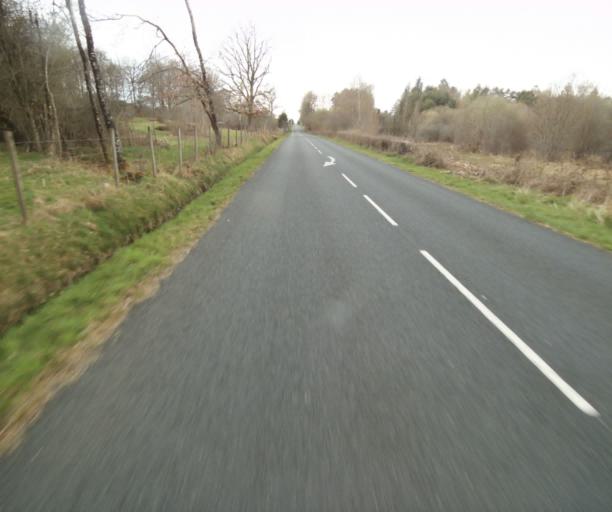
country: FR
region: Limousin
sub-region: Departement de la Correze
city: Egletons
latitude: 45.2772
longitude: 1.9840
